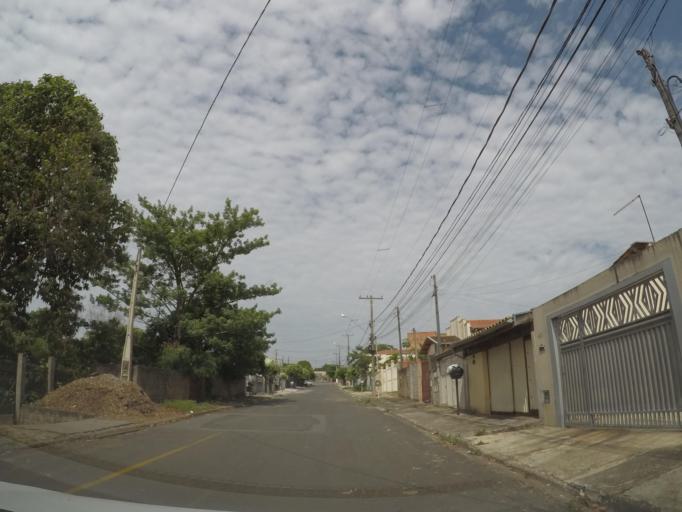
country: BR
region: Sao Paulo
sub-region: Hortolandia
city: Hortolandia
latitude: -22.8389
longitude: -47.1869
